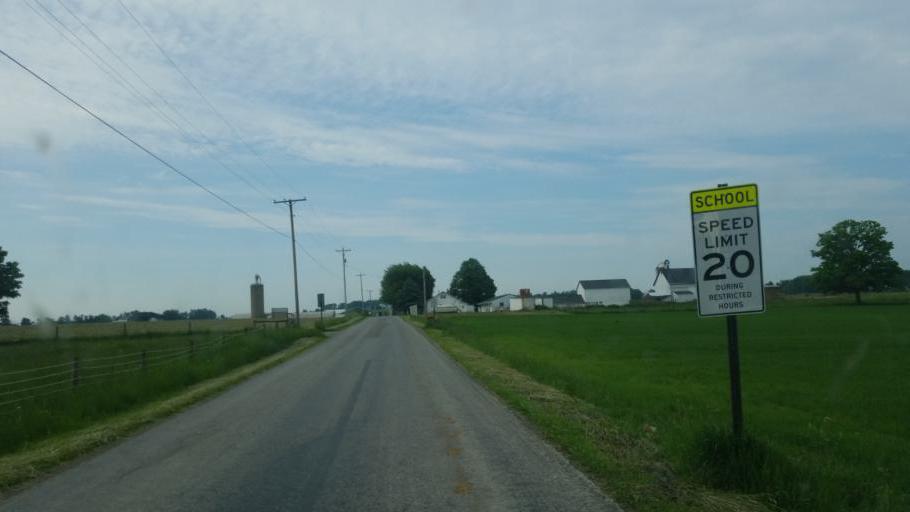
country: US
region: Ohio
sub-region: Wayne County
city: Apple Creek
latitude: 40.7032
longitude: -81.7558
